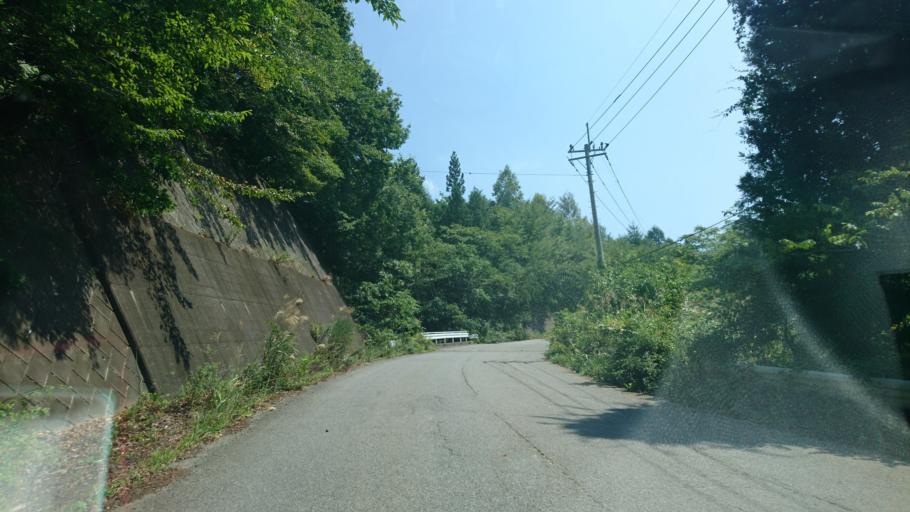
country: JP
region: Gunma
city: Numata
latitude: 36.7639
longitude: 139.2481
